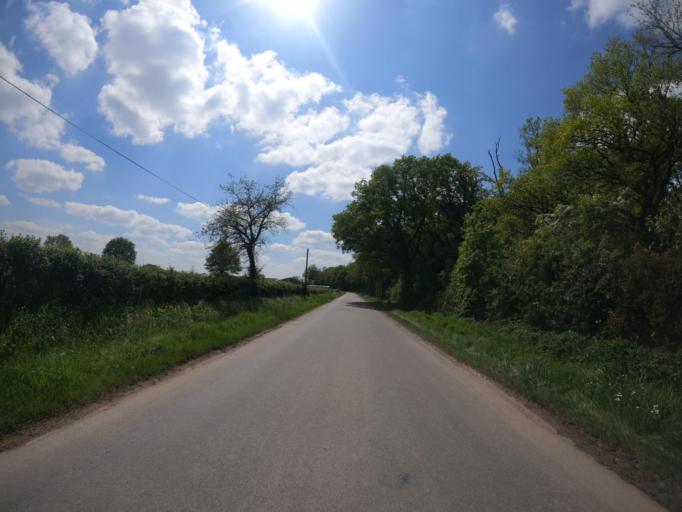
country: FR
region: Poitou-Charentes
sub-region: Departement des Deux-Sevres
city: Chiche
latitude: 46.7817
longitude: -0.3187
